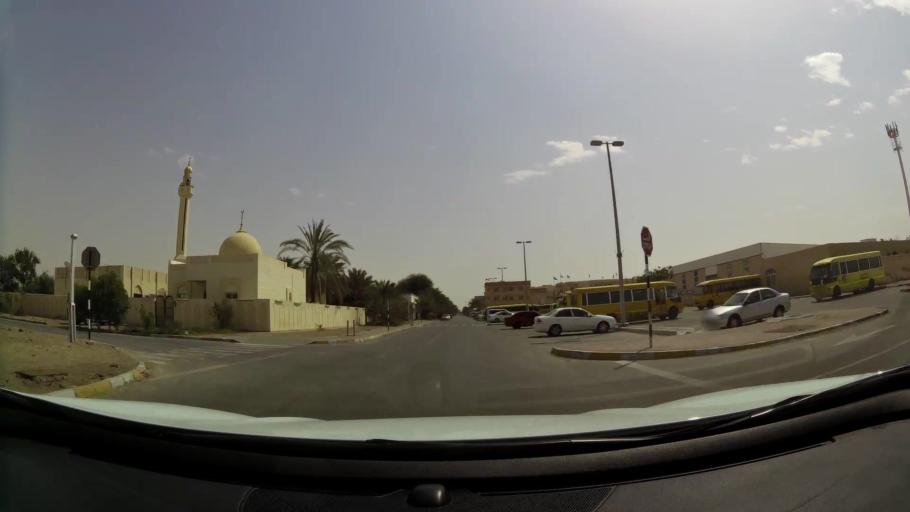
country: AE
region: Abu Dhabi
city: Abu Dhabi
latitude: 24.2947
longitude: 54.6335
